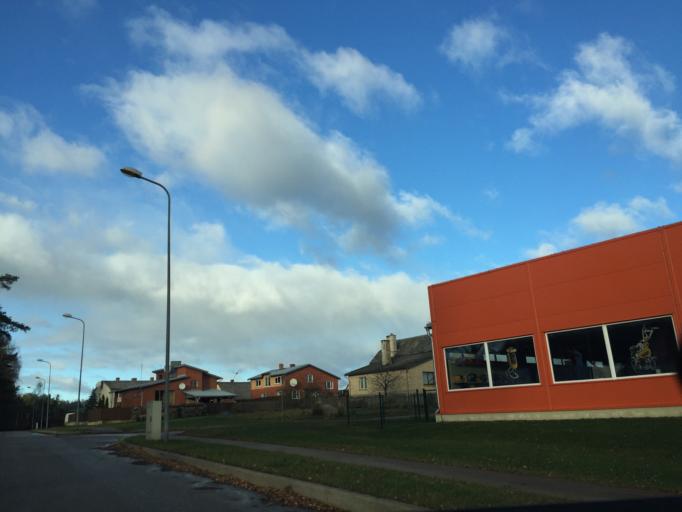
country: LV
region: Valmieras Rajons
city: Valmiera
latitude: 57.5298
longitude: 25.3848
